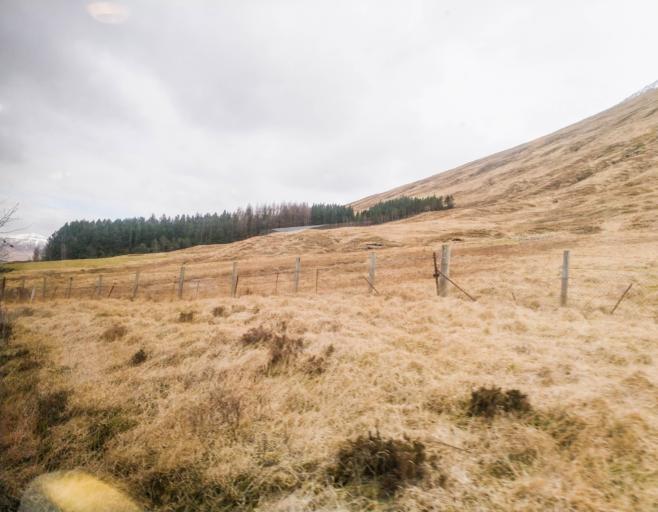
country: GB
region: Scotland
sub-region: Argyll and Bute
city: Garelochhead
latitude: 56.4955
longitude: -4.7420
